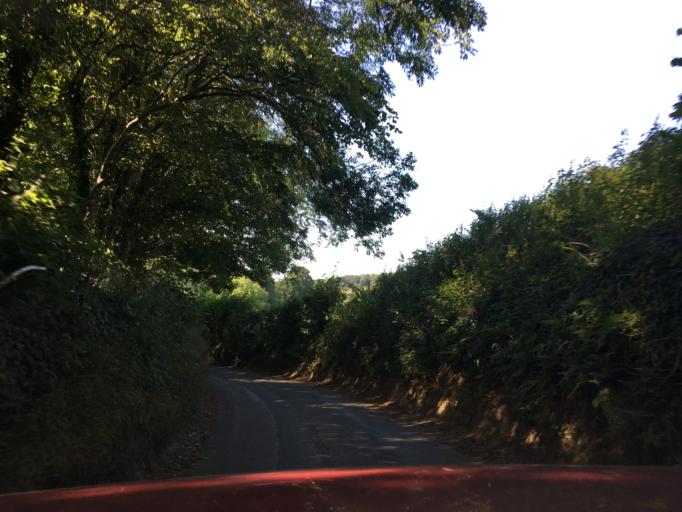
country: GB
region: England
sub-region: Gloucestershire
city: Dursley
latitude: 51.6836
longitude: -2.3180
